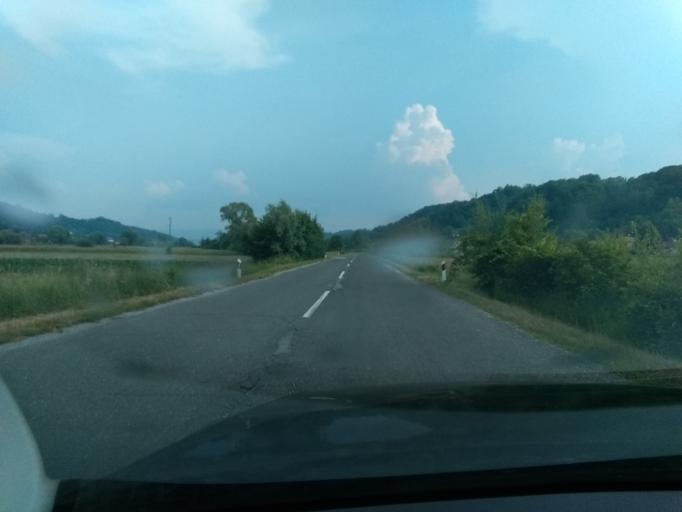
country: HR
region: Krapinsko-Zagorska
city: Pregrada
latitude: 46.0645
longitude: 15.7944
